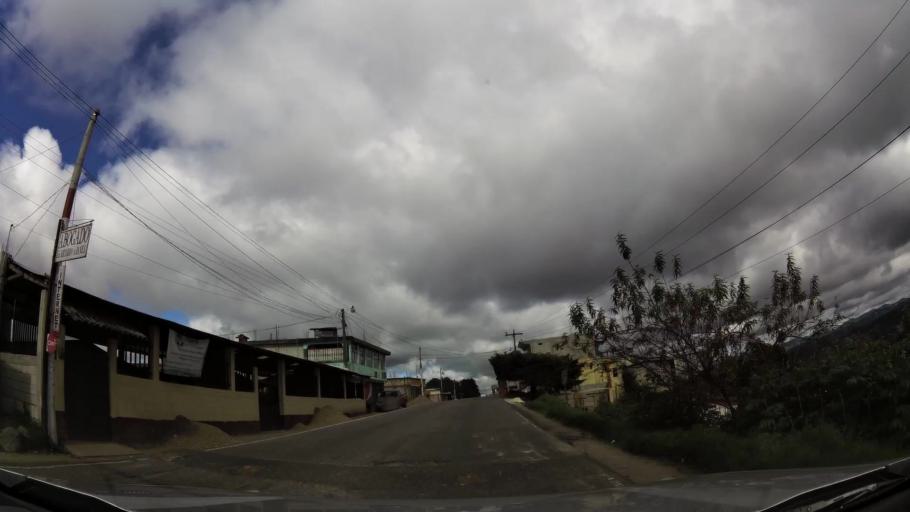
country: GT
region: Quiche
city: Chichicastenango
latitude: 14.8822
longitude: -91.1281
